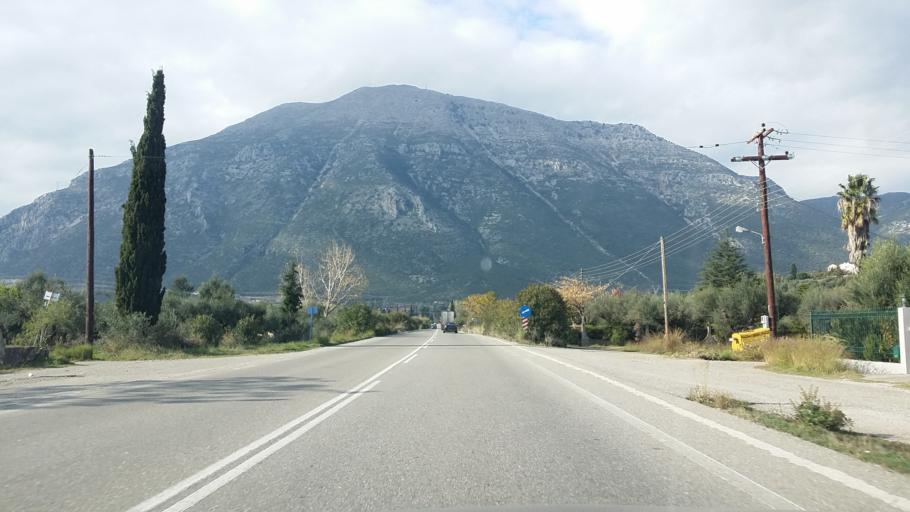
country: GR
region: West Greece
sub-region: Nomos Aitolias kai Akarnanias
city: Antirrio
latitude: 38.3481
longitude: 21.7189
